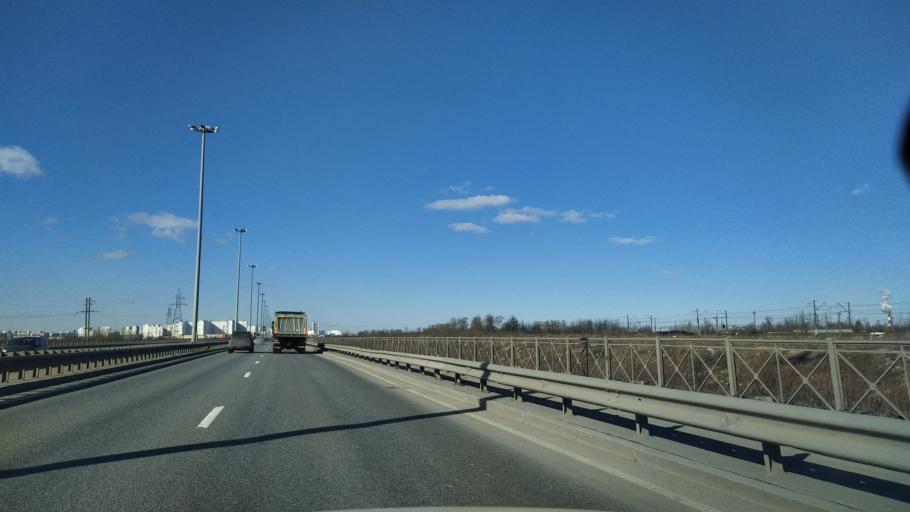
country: RU
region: St.-Petersburg
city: Shushary
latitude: 59.7780
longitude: 30.3998
